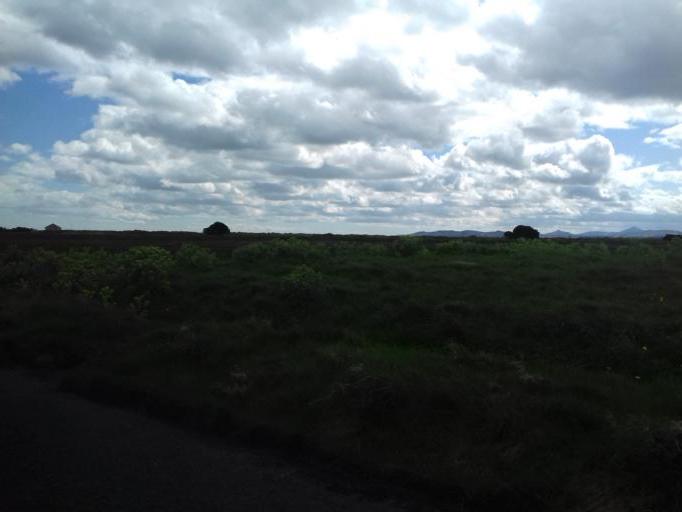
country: IE
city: Bayside
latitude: 53.3723
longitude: -6.1566
